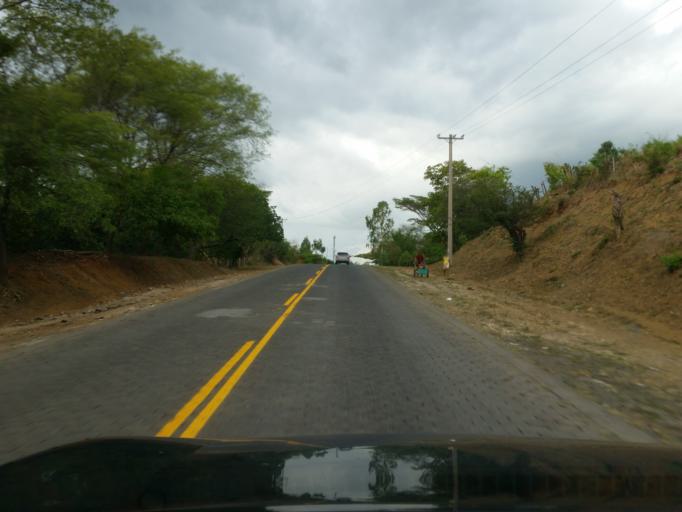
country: NI
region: Managua
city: San Rafael del Sur
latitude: 11.8928
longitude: -86.5138
